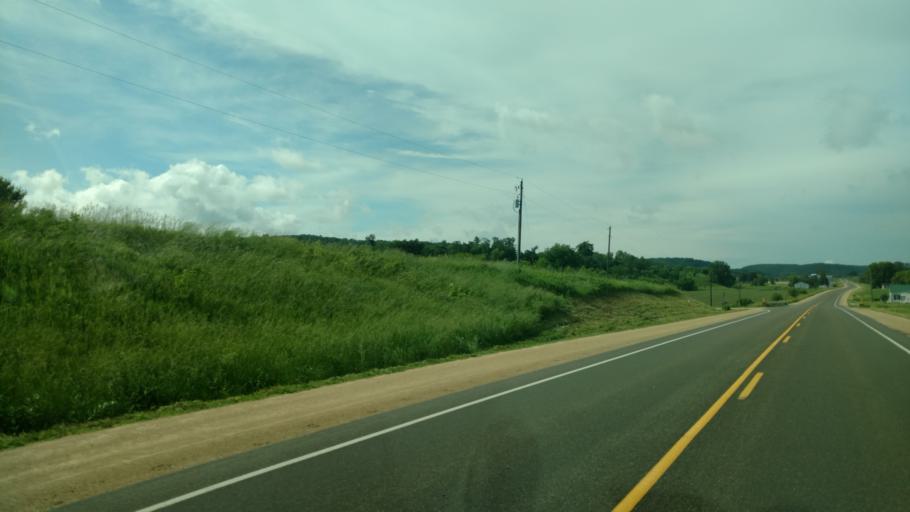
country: US
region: Wisconsin
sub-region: Monroe County
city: Tomah
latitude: 43.8374
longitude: -90.4740
